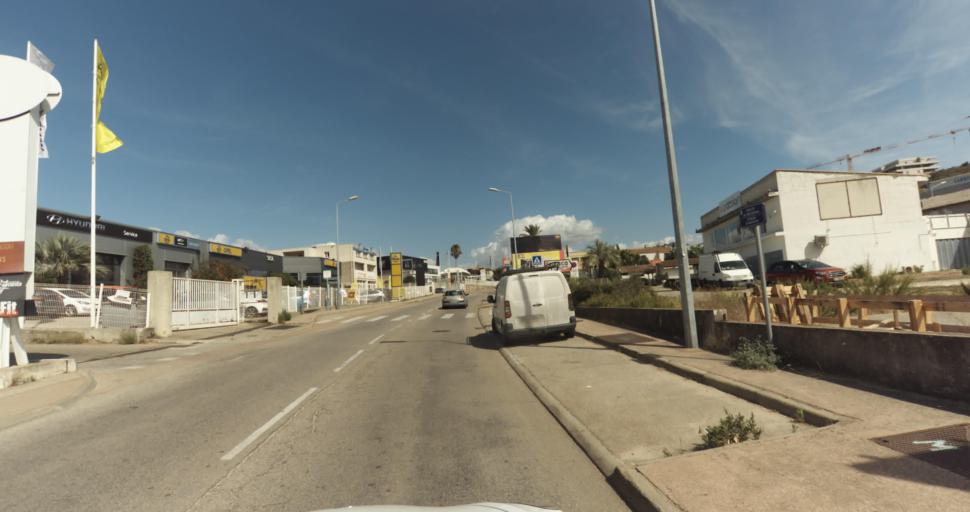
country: FR
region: Corsica
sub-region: Departement de la Corse-du-Sud
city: Alata
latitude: 41.9489
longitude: 8.7666
